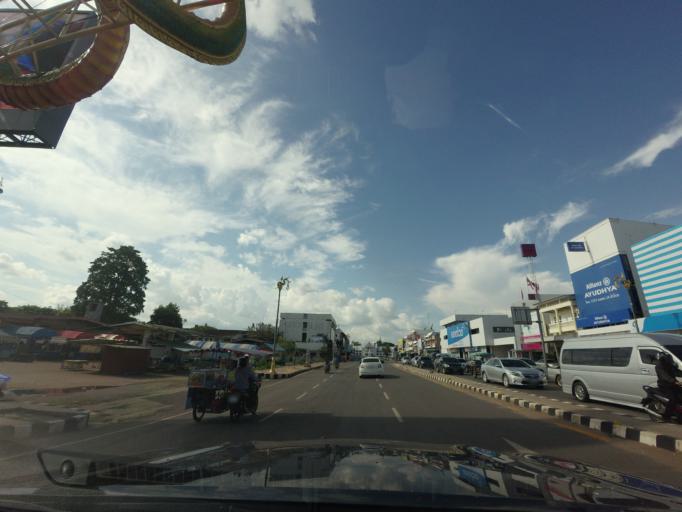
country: TH
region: Nong Khai
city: Nong Khai
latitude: 17.8767
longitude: 102.7419
